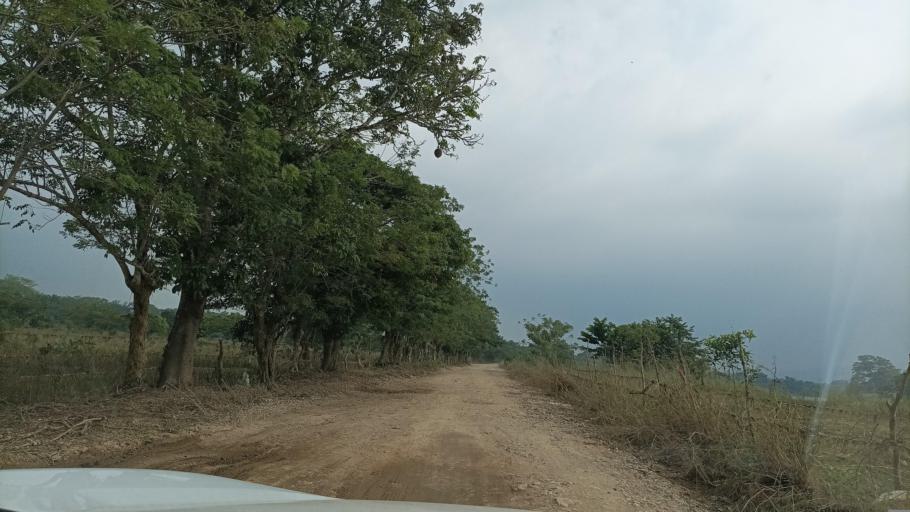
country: MX
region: Veracruz
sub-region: Moloacan
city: Cuichapa
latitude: 17.5836
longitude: -94.2174
